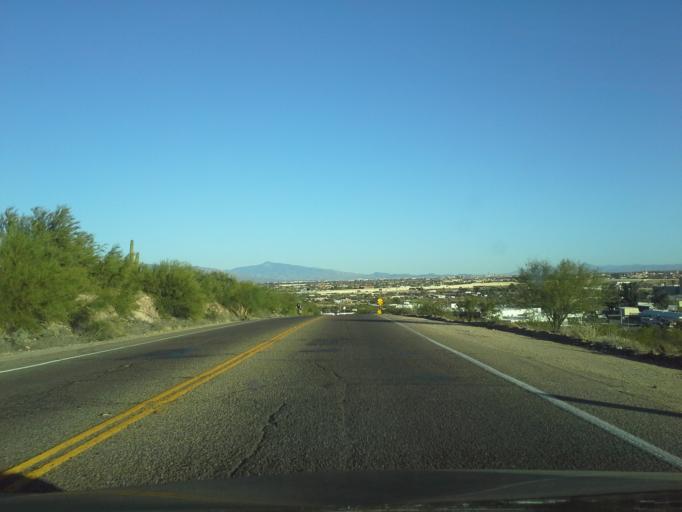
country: US
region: Arizona
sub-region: Pima County
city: South Tucson
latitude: 32.2065
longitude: -110.9973
